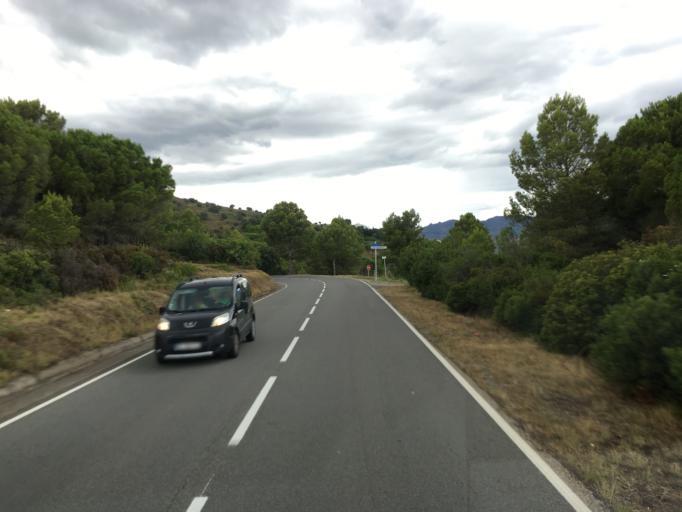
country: ES
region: Catalonia
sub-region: Provincia de Girona
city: Llanca
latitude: 42.3497
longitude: 3.1793
